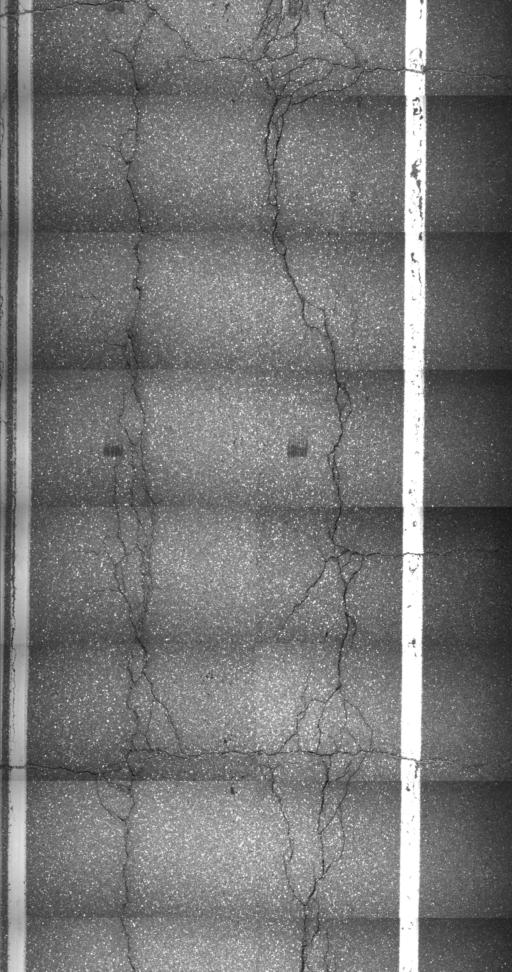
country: US
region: Vermont
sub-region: Windsor County
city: Woodstock
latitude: 43.5859
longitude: -72.4488
